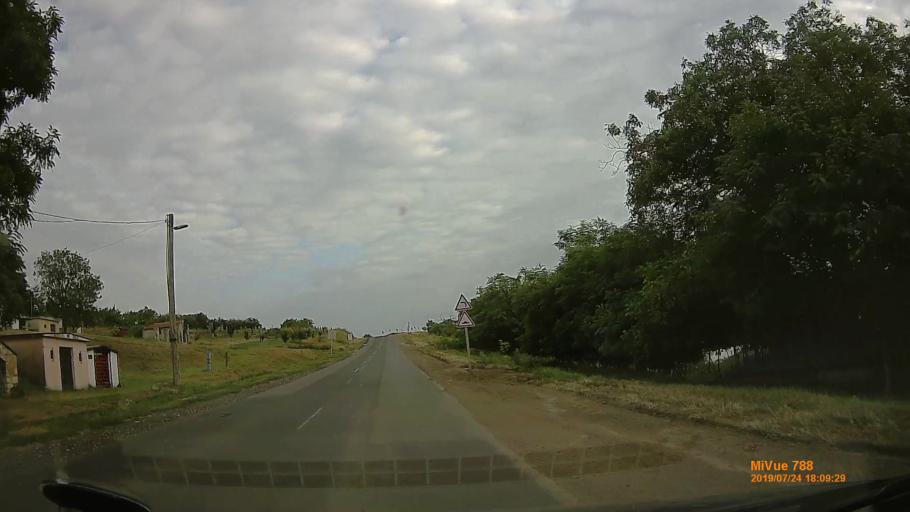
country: HU
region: Borsod-Abauj-Zemplen
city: Abaujszanto
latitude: 48.2688
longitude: 21.1834
